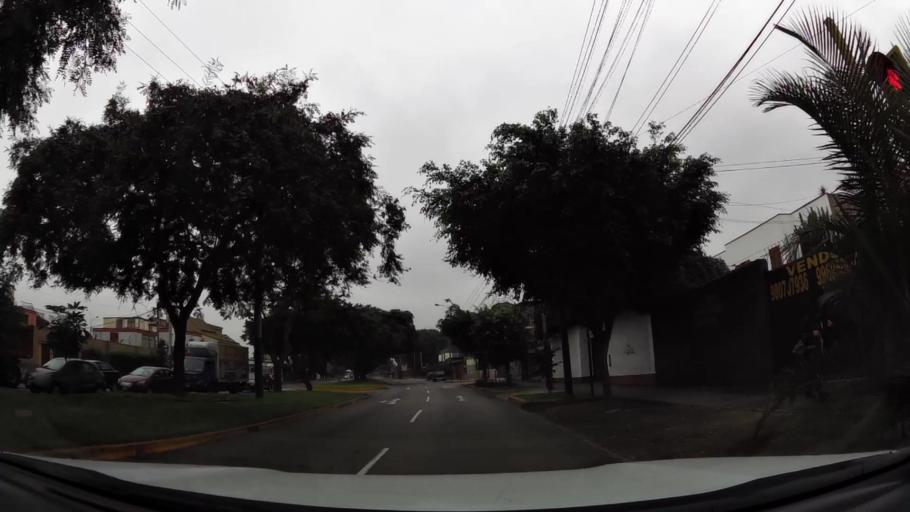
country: PE
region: Lima
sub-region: Lima
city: Surco
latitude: -12.1393
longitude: -76.9993
